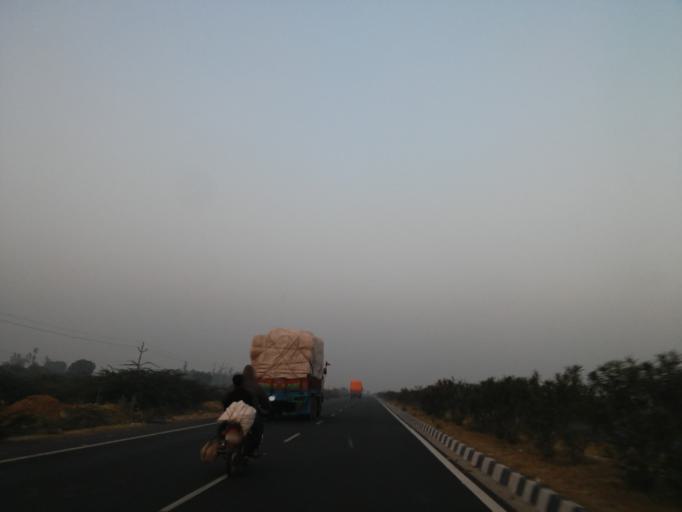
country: IN
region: Gujarat
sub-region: Surendranagar
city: Halvad
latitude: 23.0100
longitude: 71.2477
